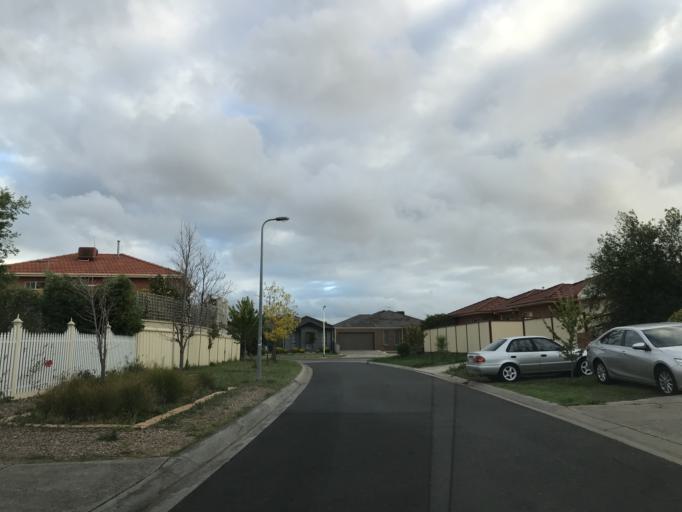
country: AU
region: Victoria
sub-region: Brimbank
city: Sunshine West
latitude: -37.7976
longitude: 144.8023
